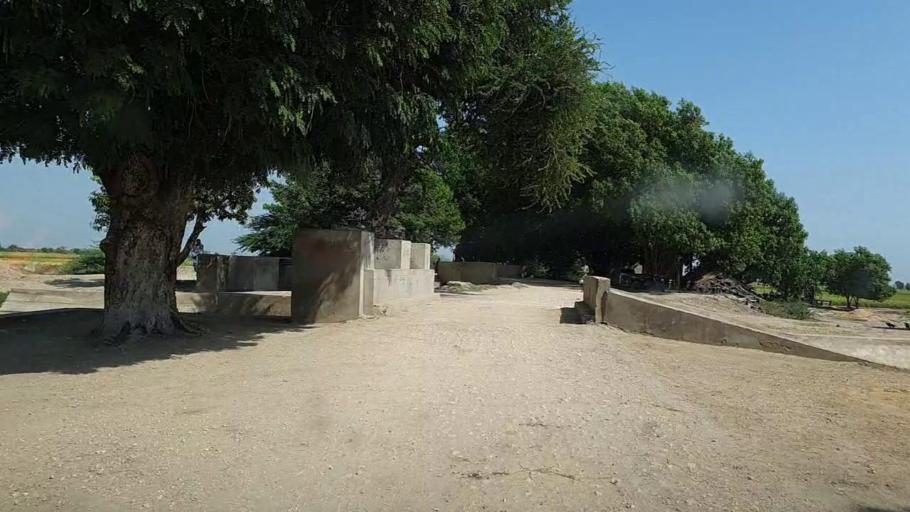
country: PK
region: Sindh
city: Kario
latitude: 24.7140
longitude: 68.4465
